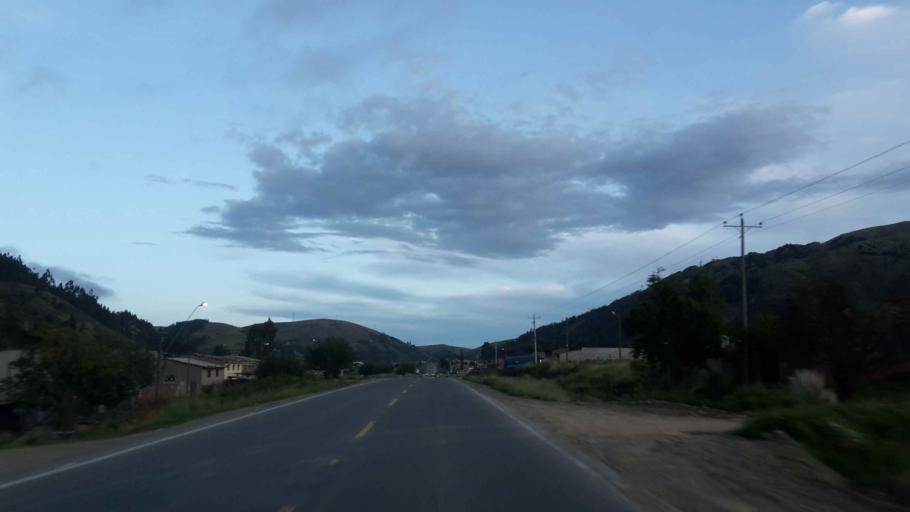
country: BO
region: Cochabamba
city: Colomi
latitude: -17.3519
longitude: -65.8523
